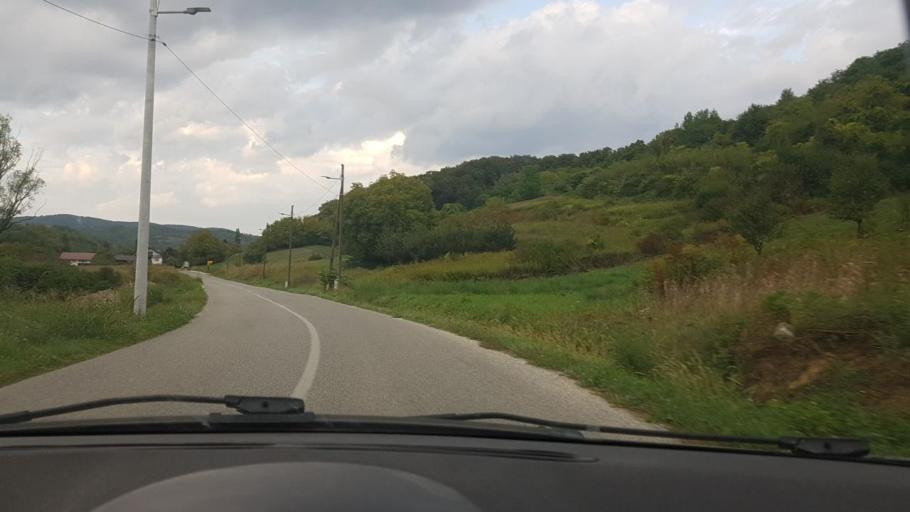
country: HR
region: Grad Zagreb
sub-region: Sesvete
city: Sesvete
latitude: 45.9142
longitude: 16.1693
